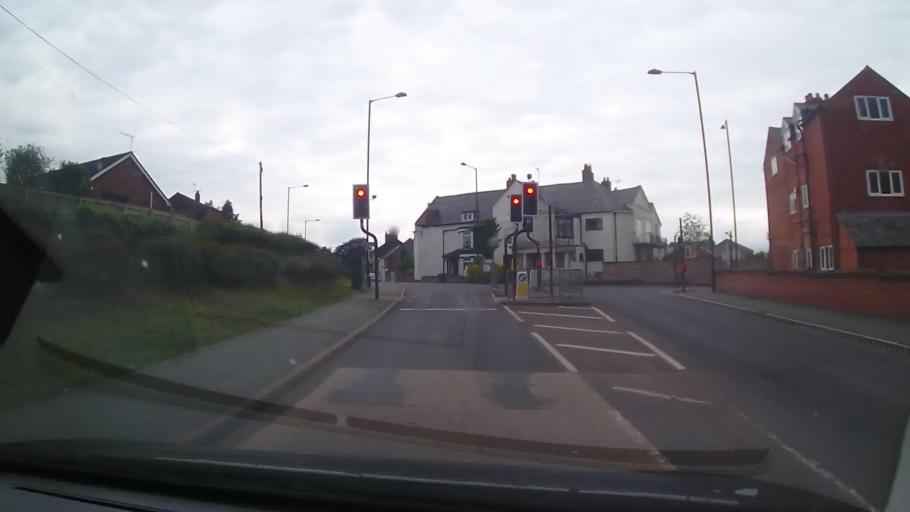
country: GB
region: England
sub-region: Shropshire
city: Ellesmere
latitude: 52.9054
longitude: -2.8984
